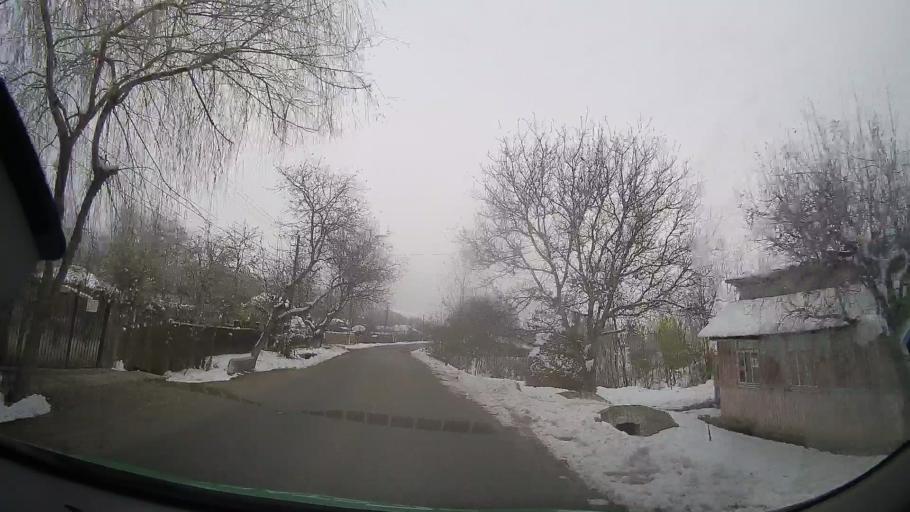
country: RO
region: Bacau
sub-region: Comuna Stanisesti
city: Stanisesti
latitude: 46.4177
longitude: 27.2677
